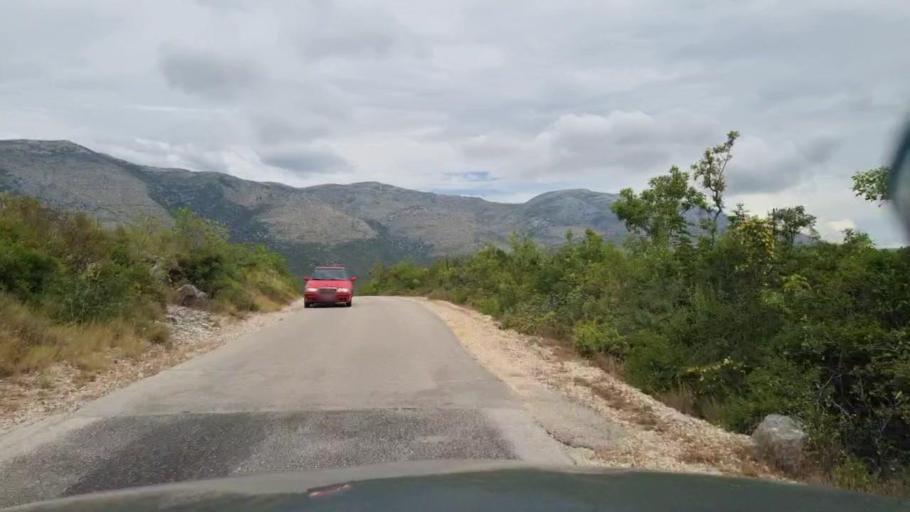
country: BA
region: Federation of Bosnia and Herzegovina
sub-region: Hercegovacko-Bosanski Kanton
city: Neum
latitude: 42.9466
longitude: 17.7016
